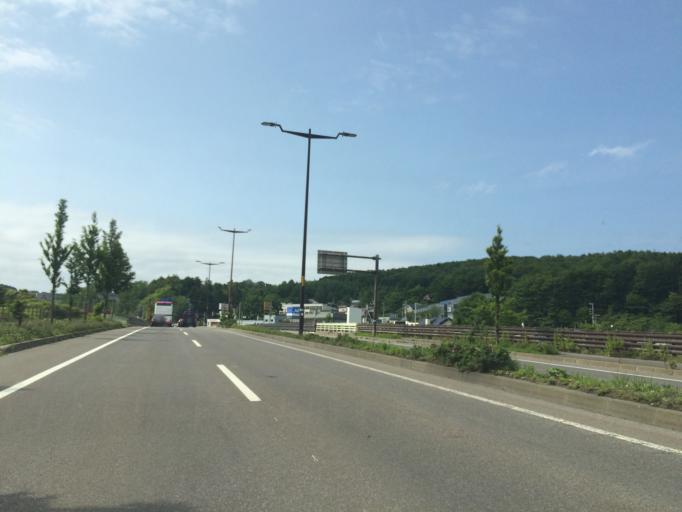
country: JP
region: Hokkaido
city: Otaru
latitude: 43.2169
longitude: 140.9556
